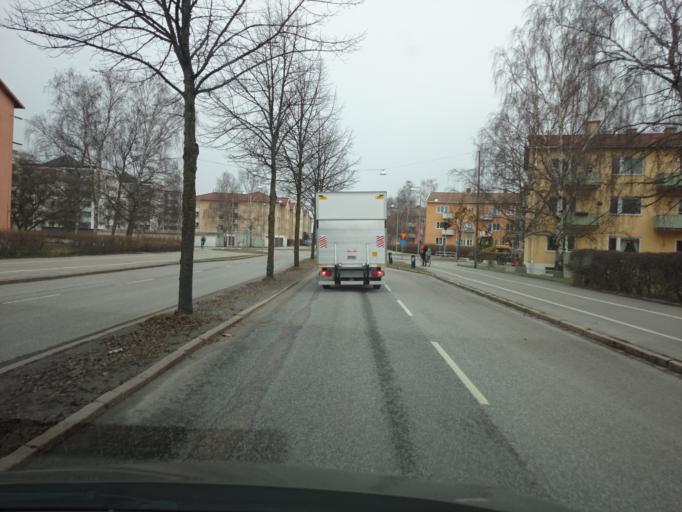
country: SE
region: Uppsala
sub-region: Uppsala Kommun
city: Uppsala
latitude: 59.8720
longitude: 17.6266
